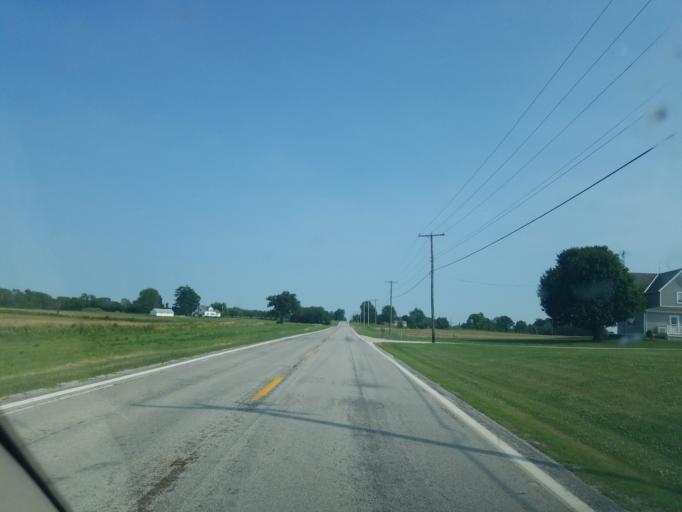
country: US
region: Ohio
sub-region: Wyandot County
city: Carey
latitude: 41.0388
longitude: -83.3070
